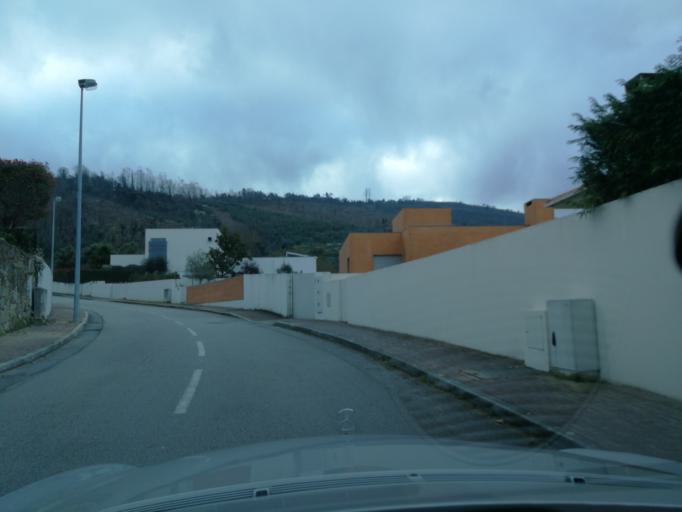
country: PT
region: Braga
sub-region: Braga
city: Braga
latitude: 41.5429
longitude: -8.3926
